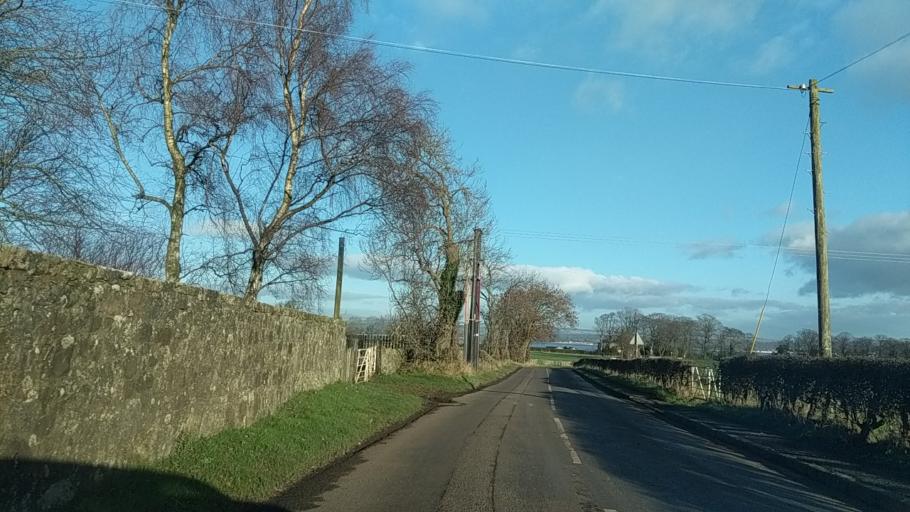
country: GB
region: Scotland
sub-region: Fife
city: Crossford
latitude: 56.0005
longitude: -3.5283
